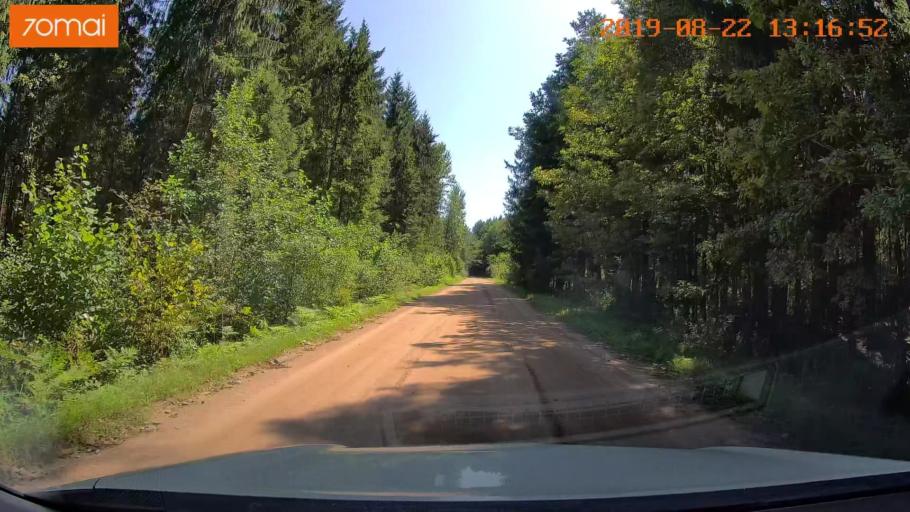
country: BY
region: Minsk
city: Prawdzinski
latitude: 53.2526
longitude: 27.9156
